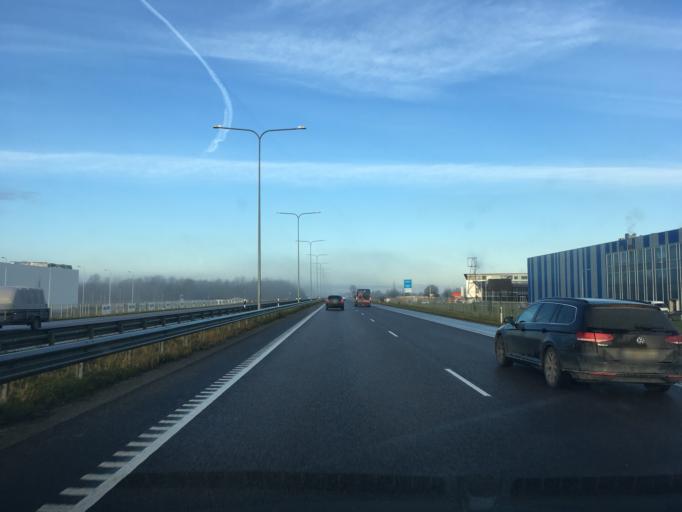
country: EE
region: Harju
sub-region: Rae vald
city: Jueri
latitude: 59.3640
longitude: 24.8661
